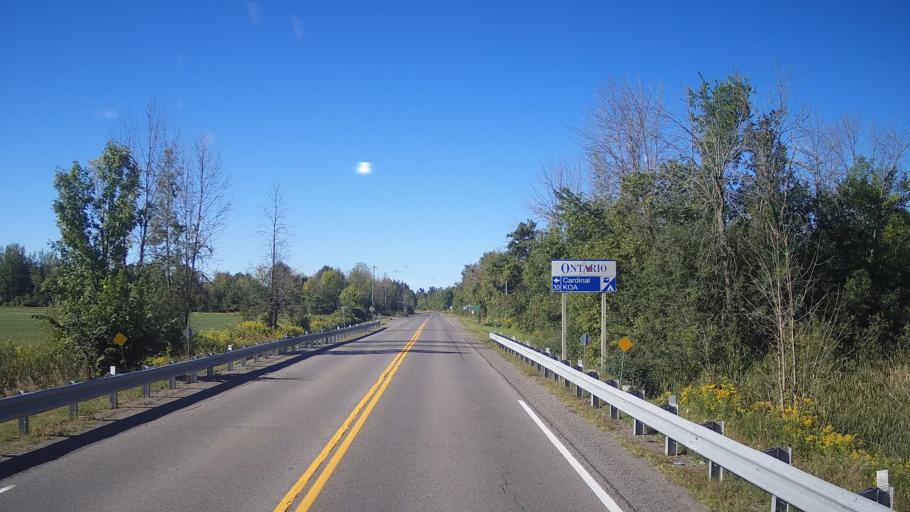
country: CA
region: Ontario
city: Bells Corners
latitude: 45.0903
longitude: -75.6276
